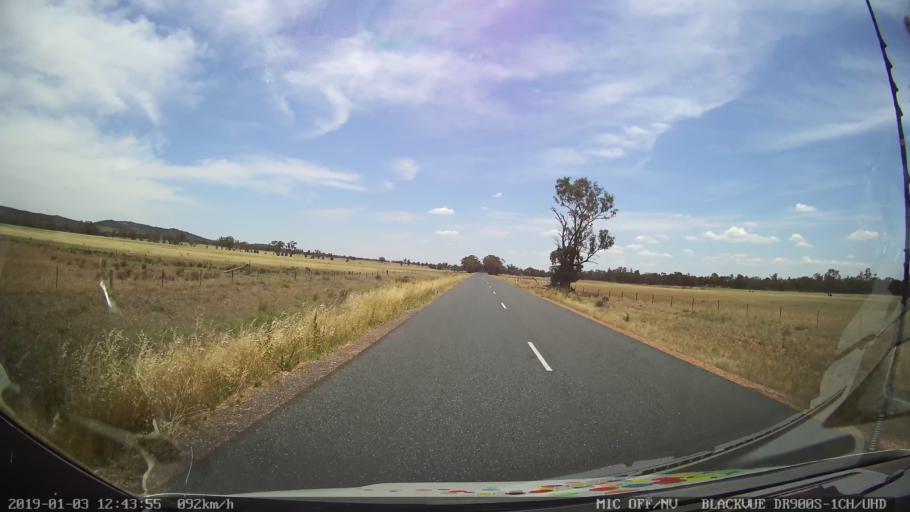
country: AU
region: New South Wales
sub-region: Weddin
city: Grenfell
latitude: -33.7685
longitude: 148.2145
